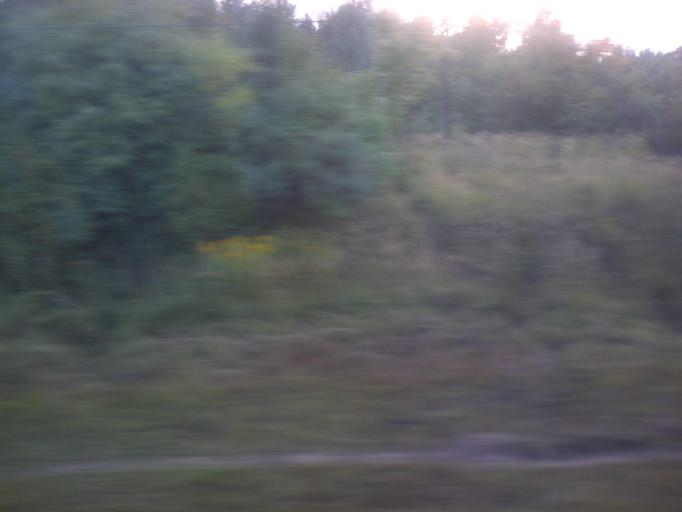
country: RU
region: Moscow
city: Tsaritsyno
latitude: 55.6076
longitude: 37.6434
